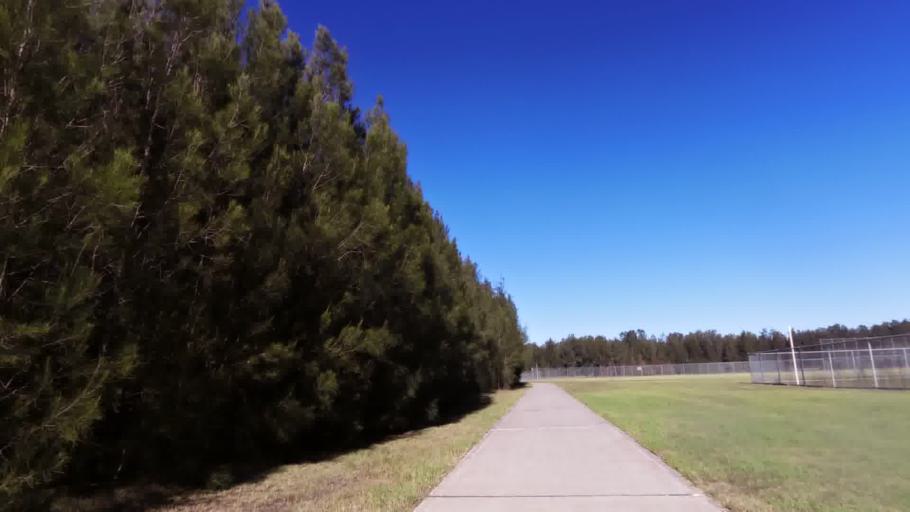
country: AU
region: New South Wales
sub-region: Wollongong
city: Berkeley
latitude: -34.4843
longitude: 150.8394
